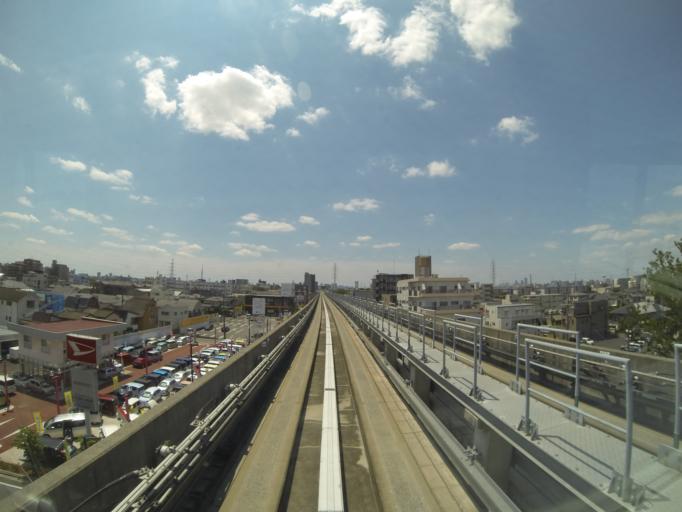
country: JP
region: Saitama
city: Soka
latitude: 35.7851
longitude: 139.7701
